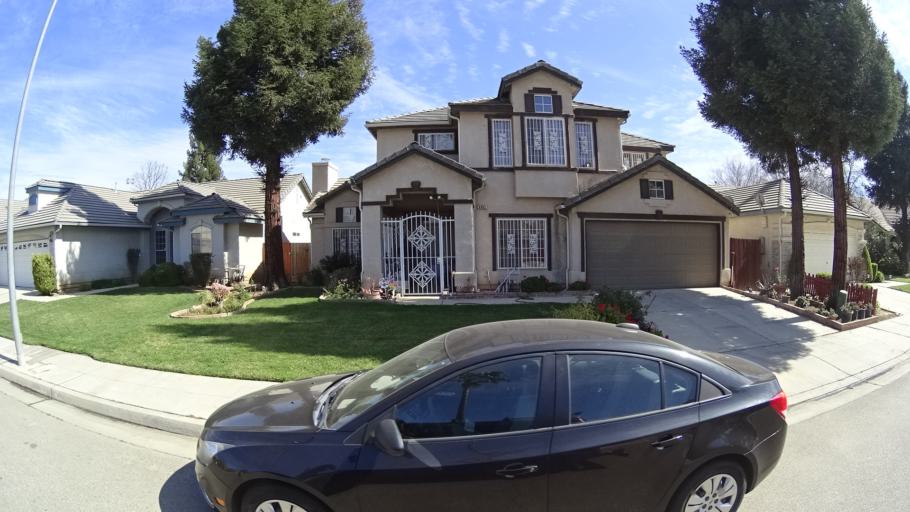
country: US
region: California
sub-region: Fresno County
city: Clovis
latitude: 36.8530
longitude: -119.7686
